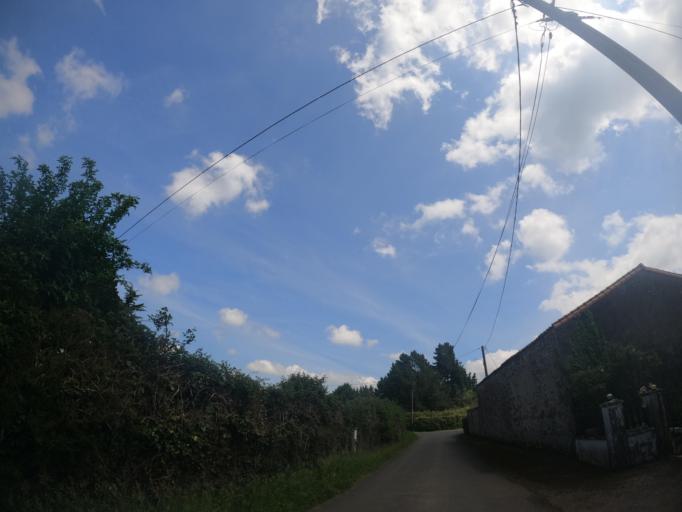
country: FR
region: Poitou-Charentes
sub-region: Departement des Deux-Sevres
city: Saint-Varent
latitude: 46.8561
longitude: -0.2053
